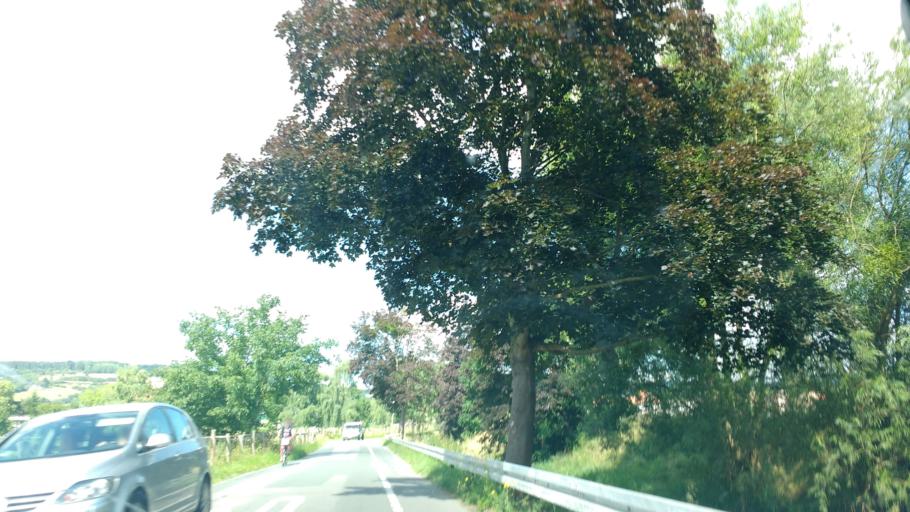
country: DE
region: Lower Saxony
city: Bad Pyrmont
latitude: 51.9796
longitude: 9.2448
